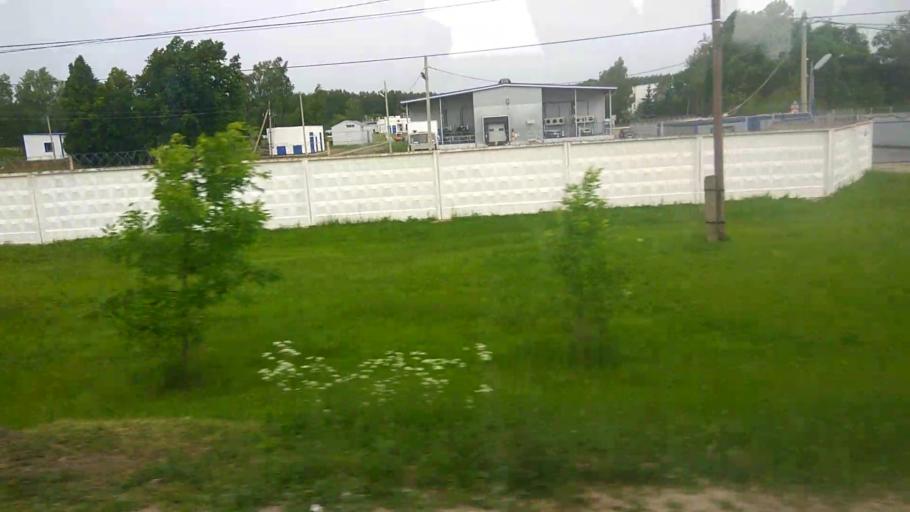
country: RU
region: Moskovskaya
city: Lukhovitsy
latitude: 54.9255
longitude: 38.9978
